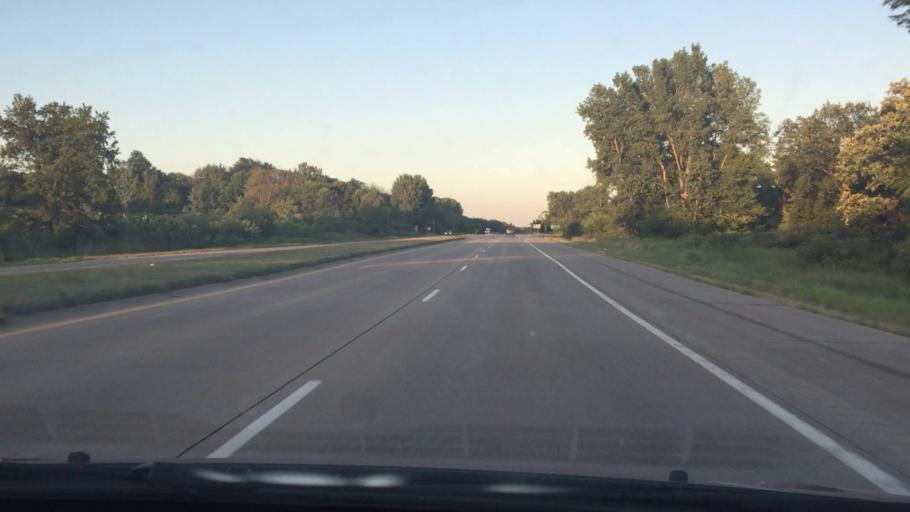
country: US
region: Iowa
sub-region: Muscatine County
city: Muscatine
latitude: 41.4527
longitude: -91.0632
